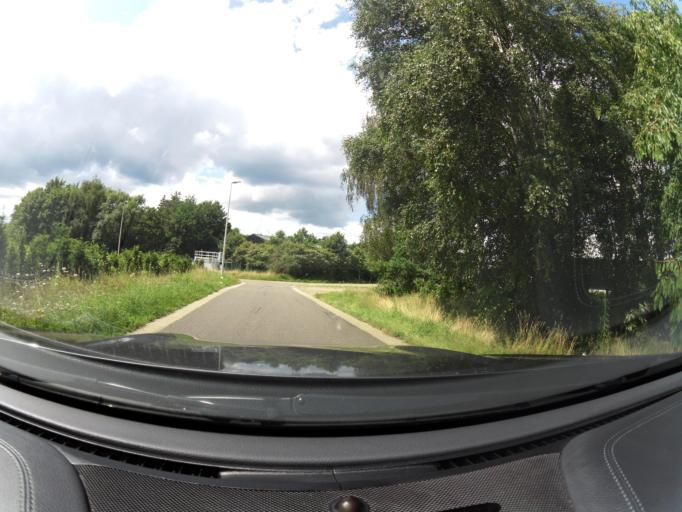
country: BE
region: Flanders
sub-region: Provincie Limburg
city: Tessenderlo
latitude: 51.0644
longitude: 5.1086
